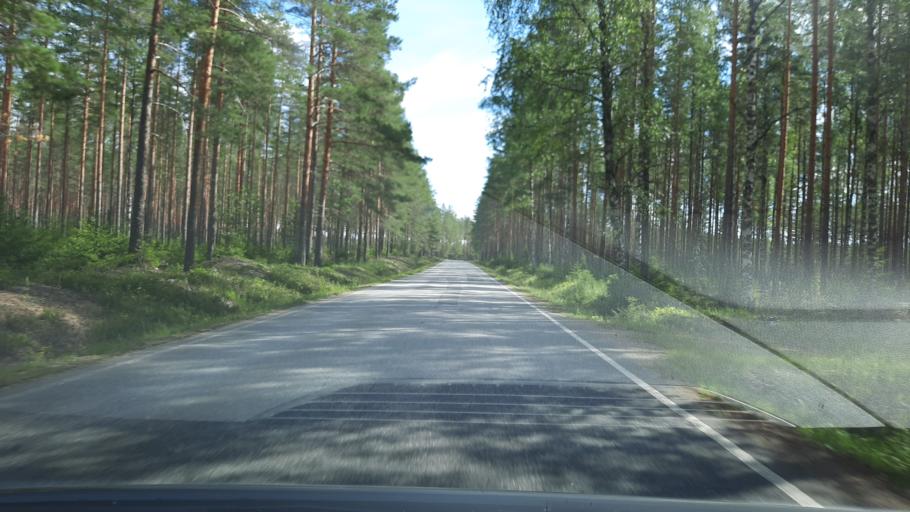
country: FI
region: Pirkanmaa
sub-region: Etelae-Pirkanmaa
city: Urjala
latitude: 61.1706
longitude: 23.3935
